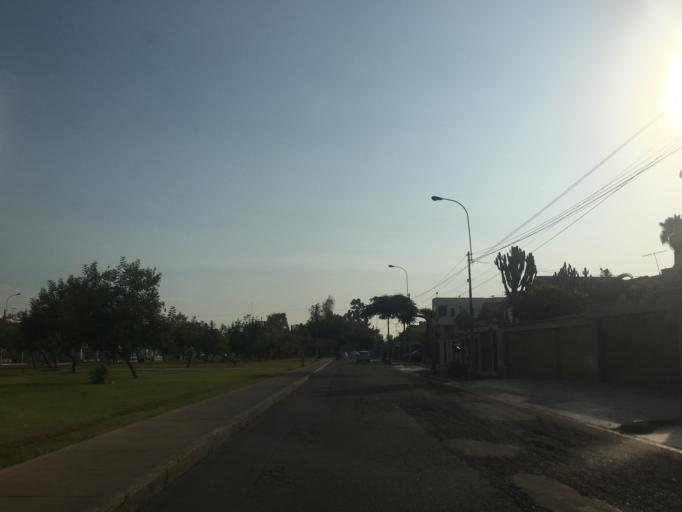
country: PE
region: Lima
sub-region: Lima
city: La Molina
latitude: -12.0698
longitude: -76.9525
